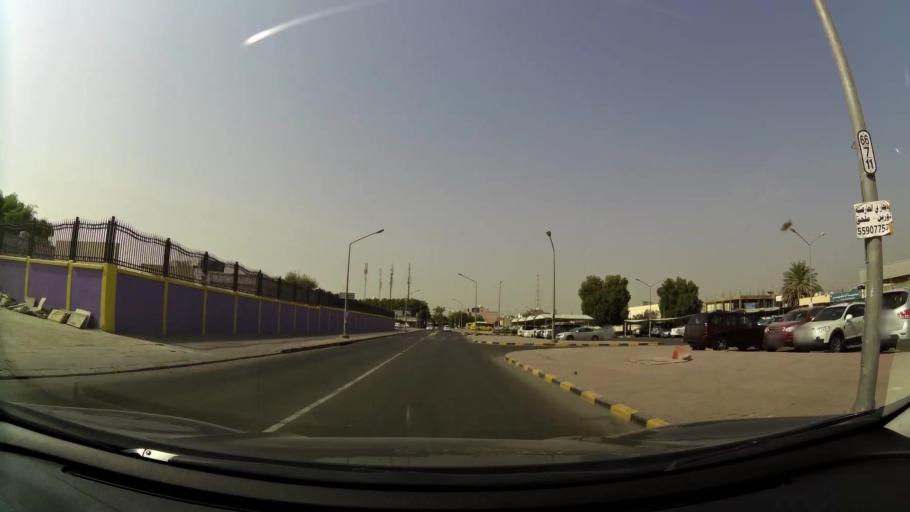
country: KW
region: Al Asimah
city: Ar Rabiyah
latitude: 29.2877
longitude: 47.8915
